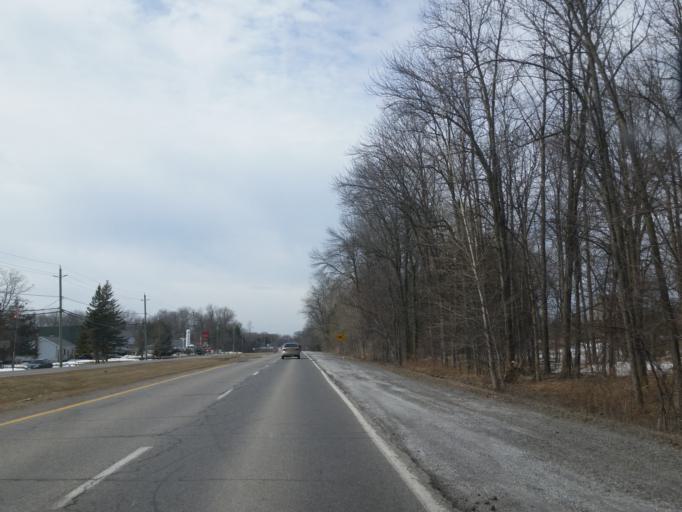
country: CA
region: Ontario
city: Belleville
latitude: 44.1709
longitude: -77.3231
